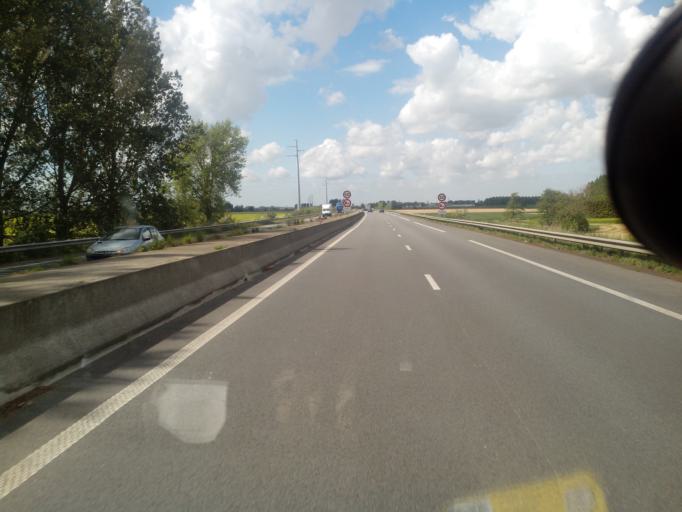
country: FR
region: Nord-Pas-de-Calais
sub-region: Departement du Nord
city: Herzeele
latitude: 50.8919
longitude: 2.5086
